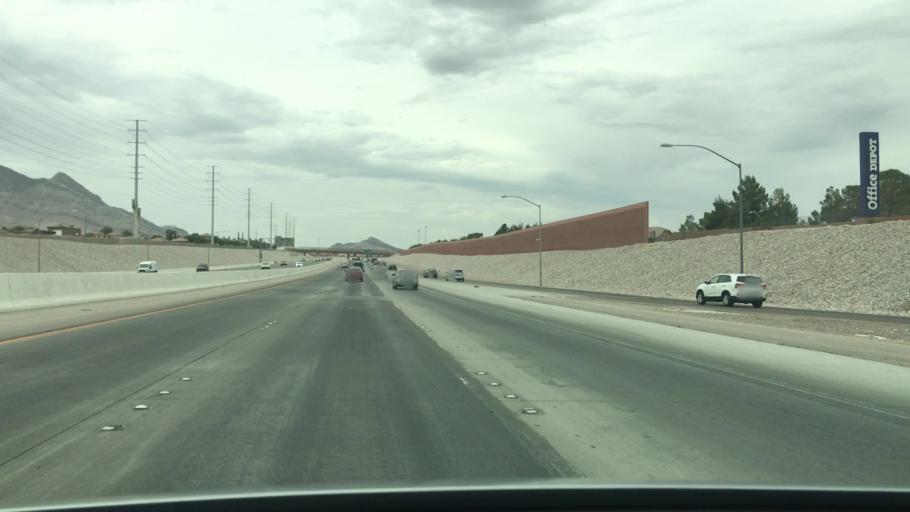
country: US
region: Nevada
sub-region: Clark County
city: Summerlin South
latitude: 36.1627
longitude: -115.3371
